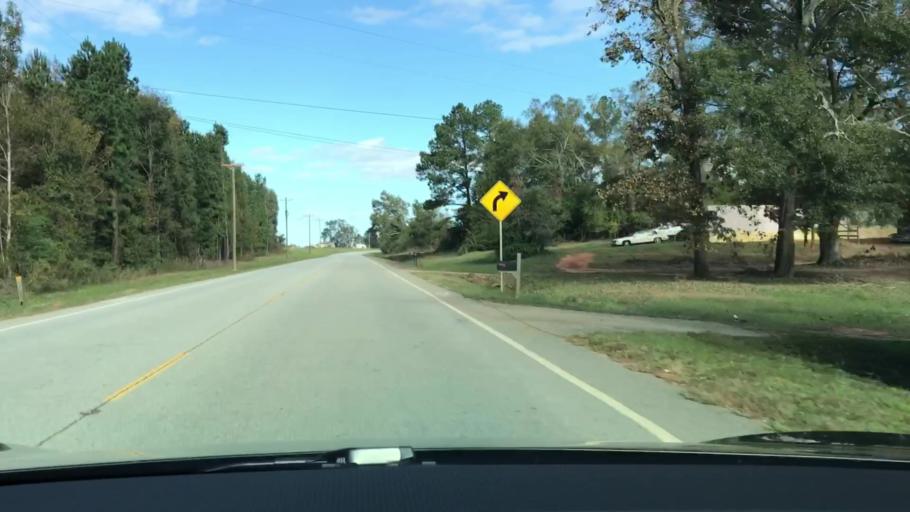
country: US
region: Georgia
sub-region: Jefferson County
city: Wrens
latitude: 33.1382
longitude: -82.4553
